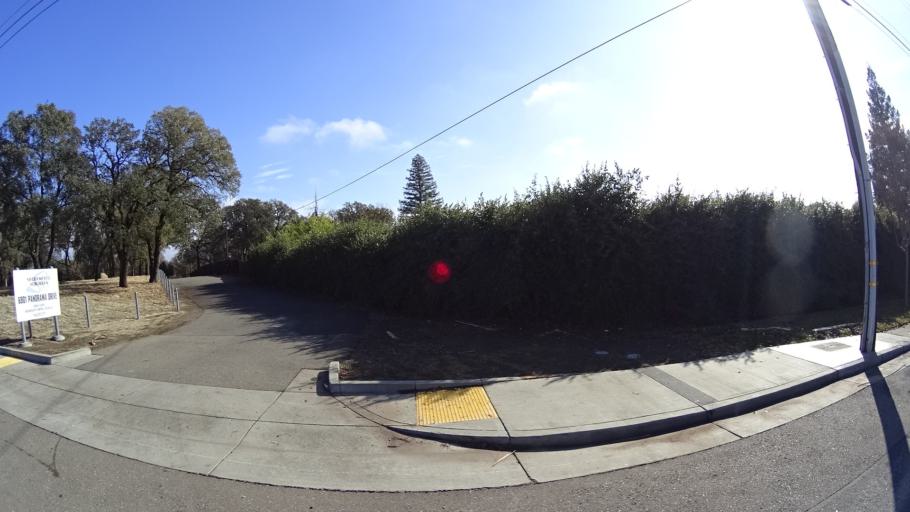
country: US
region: California
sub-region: Sacramento County
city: Antelope
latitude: 38.6897
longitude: -121.3281
